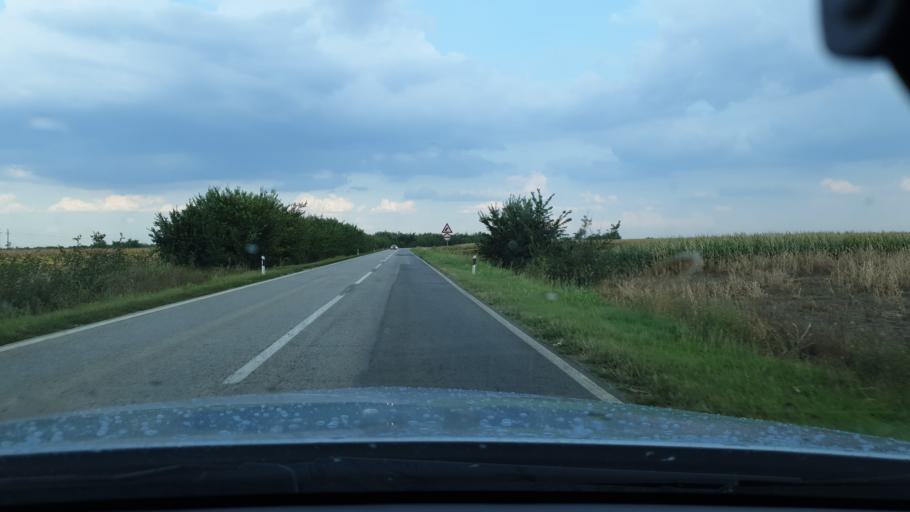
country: RS
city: Sutjeska
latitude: 45.3818
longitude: 20.7211
